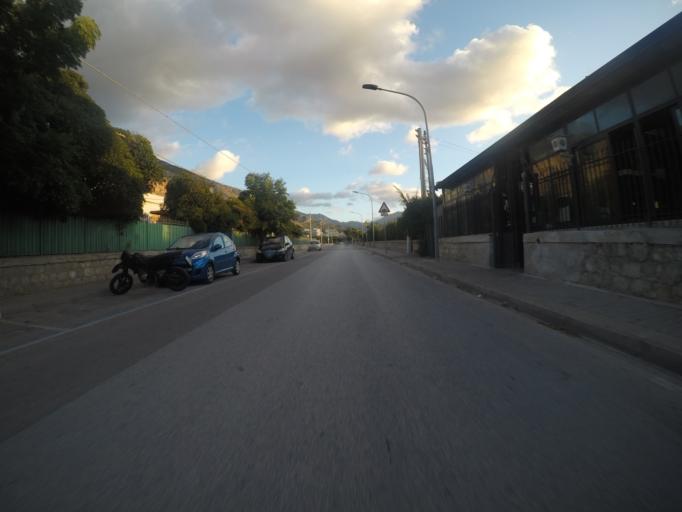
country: IT
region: Sicily
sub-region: Palermo
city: Isola delle Femmine
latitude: 38.1847
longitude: 13.2379
